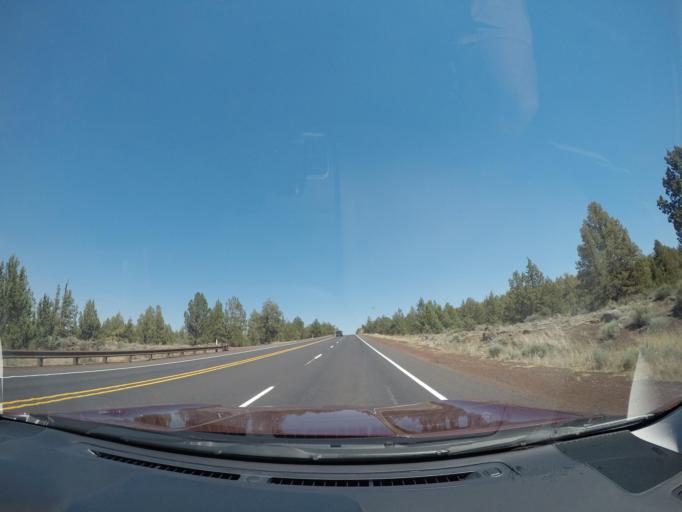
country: US
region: Oregon
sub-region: Deschutes County
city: Sisters
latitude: 44.2948
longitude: -121.3952
